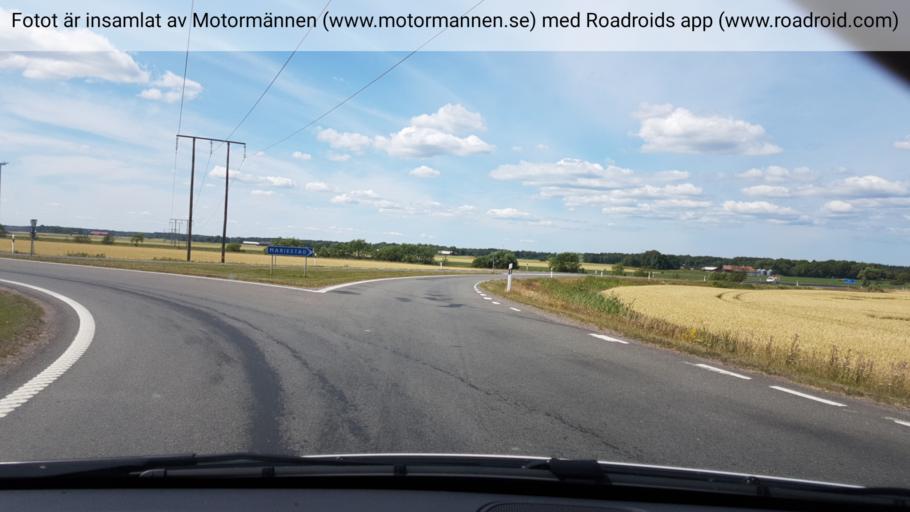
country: SE
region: Vaestra Goetaland
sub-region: Toreboda Kommun
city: Toereboda
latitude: 58.6091
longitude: 14.0102
